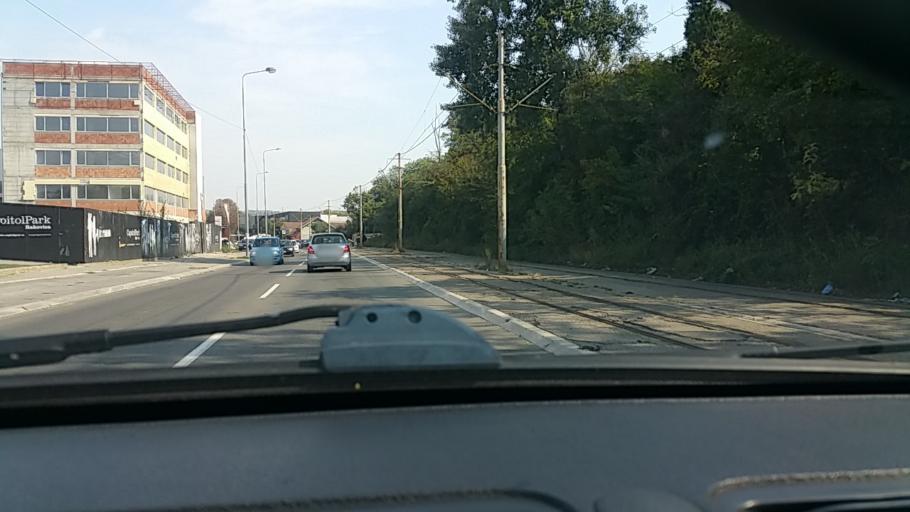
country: RS
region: Central Serbia
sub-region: Belgrade
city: Rakovica
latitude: 44.7402
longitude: 20.4396
